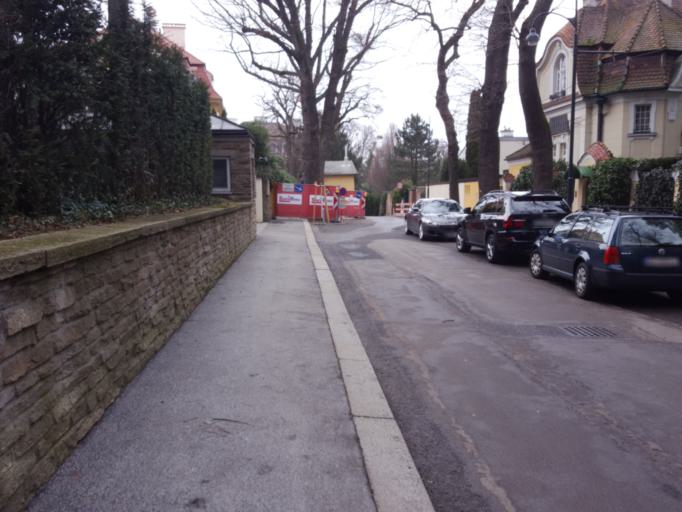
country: AT
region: Lower Austria
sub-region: Politischer Bezirk Modling
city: Perchtoldsdorf
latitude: 48.1795
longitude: 16.2981
